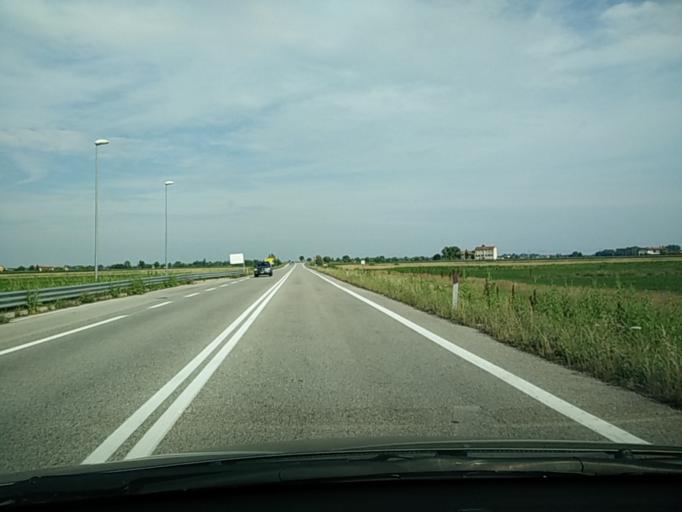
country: IT
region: Veneto
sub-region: Provincia di Venezia
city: Musile di Piave
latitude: 45.6030
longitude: 12.5210
